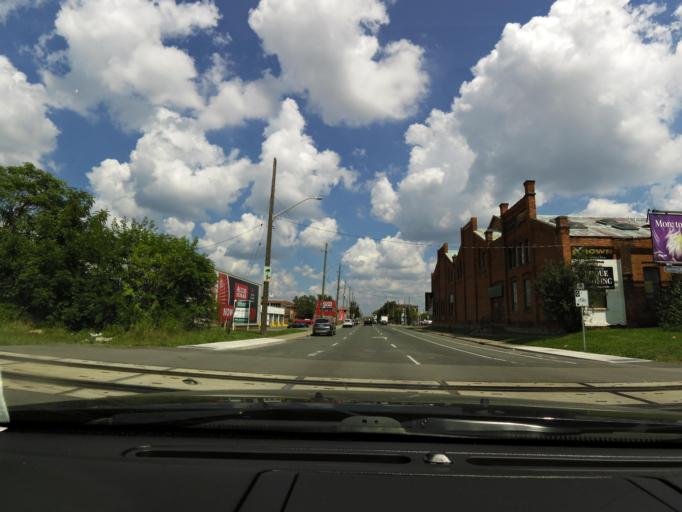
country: CA
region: Ontario
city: Hamilton
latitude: 43.2635
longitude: -79.8522
